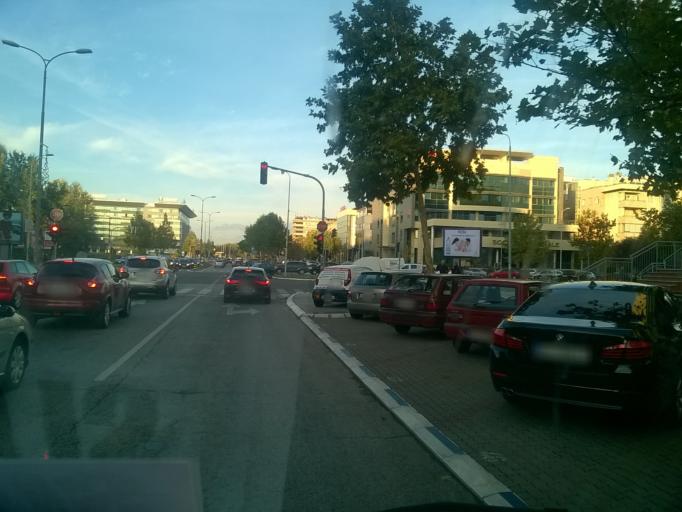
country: RS
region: Central Serbia
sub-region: Belgrade
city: Novi Beograd
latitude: 44.8138
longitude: 20.4250
